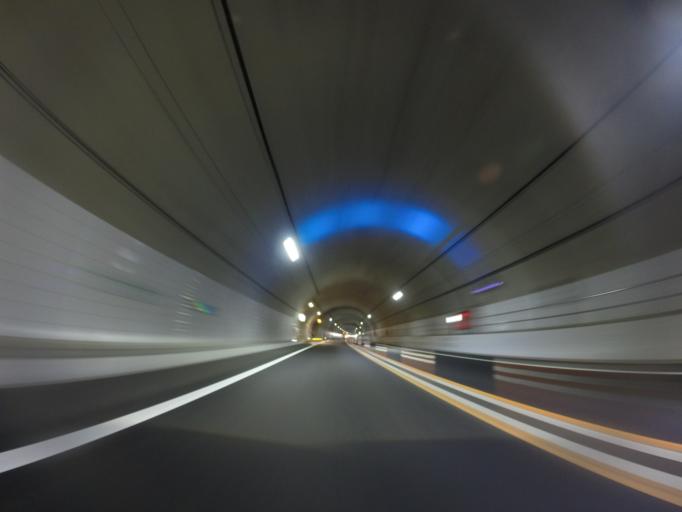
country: JP
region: Yamanashi
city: Ryuo
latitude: 35.4309
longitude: 138.4585
